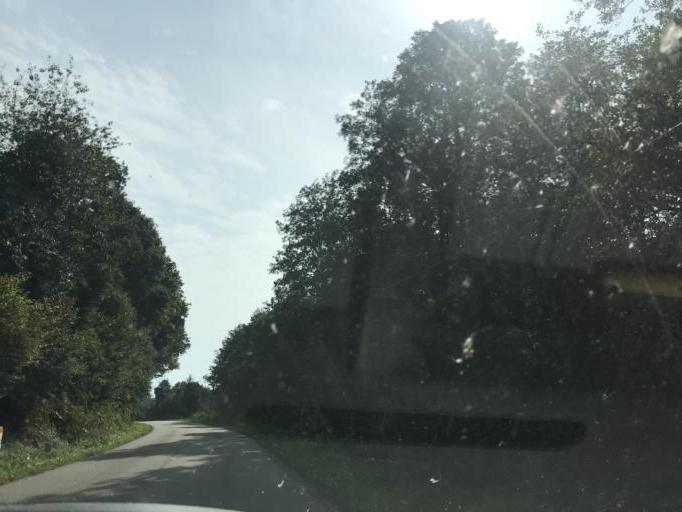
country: FR
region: Brittany
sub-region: Departement du Finistere
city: Loperec
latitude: 48.2976
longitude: -4.0181
